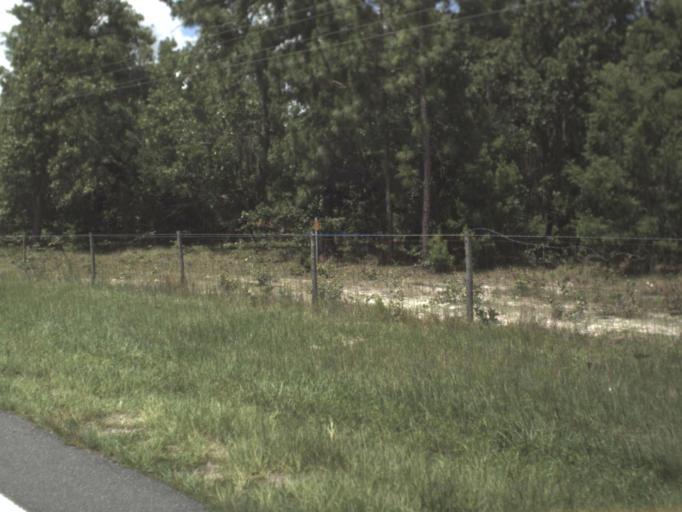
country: US
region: Florida
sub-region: Alachua County
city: Hawthorne
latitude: 29.6673
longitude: -82.0329
